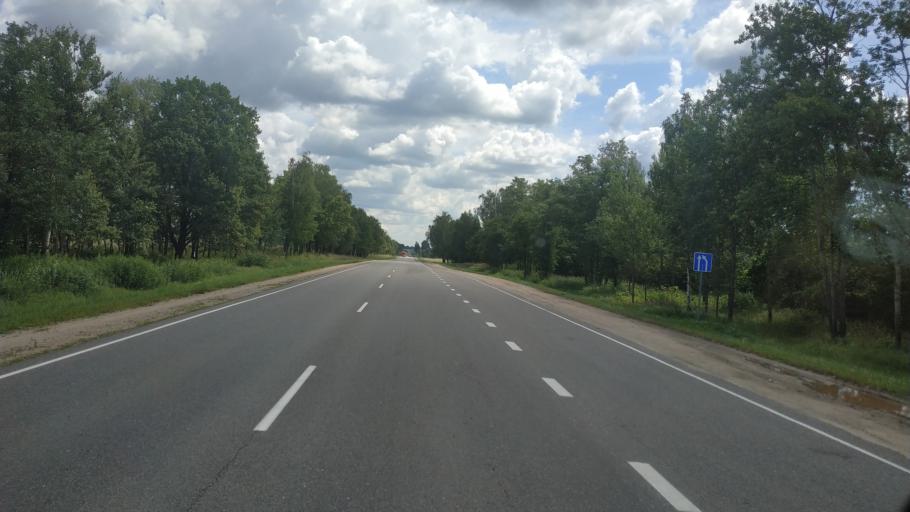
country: BY
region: Mogilev
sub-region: Mahilyowski Rayon
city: Veyno
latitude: 53.8197
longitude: 30.4374
